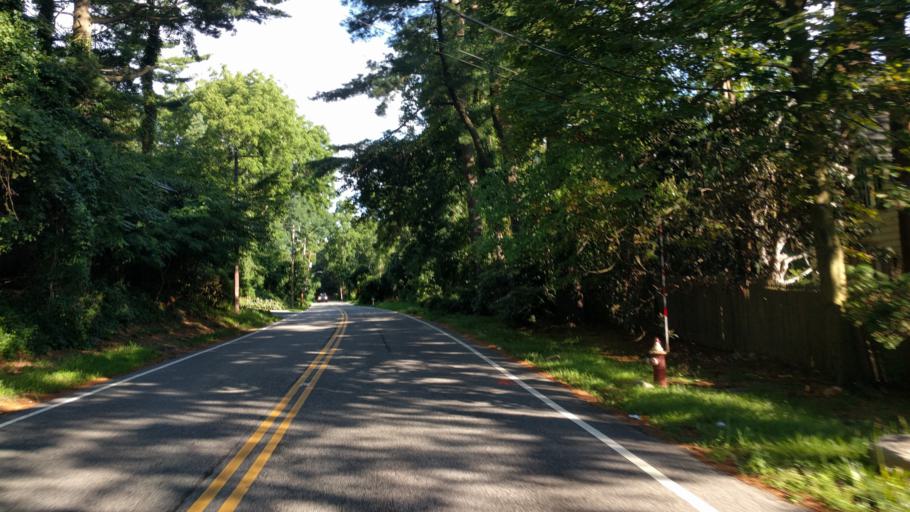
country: US
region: New York
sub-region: Nassau County
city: Oyster Bay Cove
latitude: 40.8499
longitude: -73.5085
